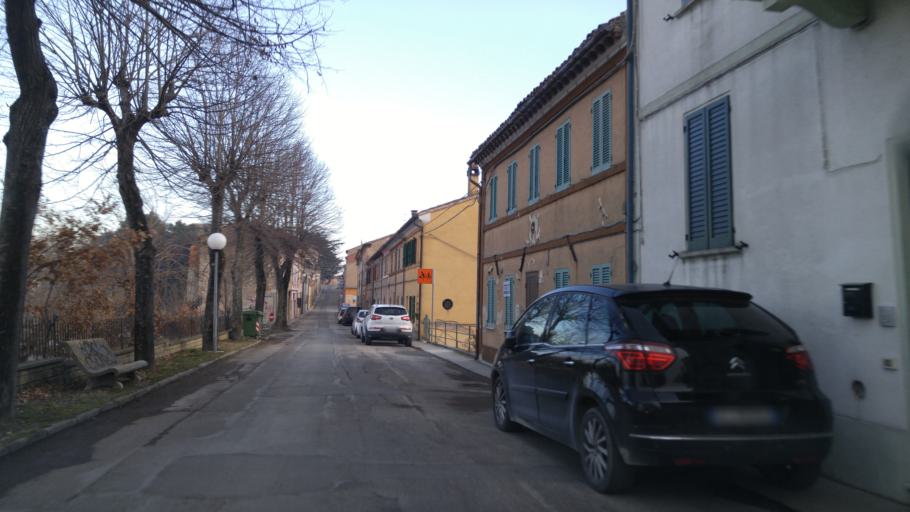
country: IT
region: The Marches
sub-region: Provincia di Pesaro e Urbino
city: Monte Porzio
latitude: 43.6920
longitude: 13.0436
